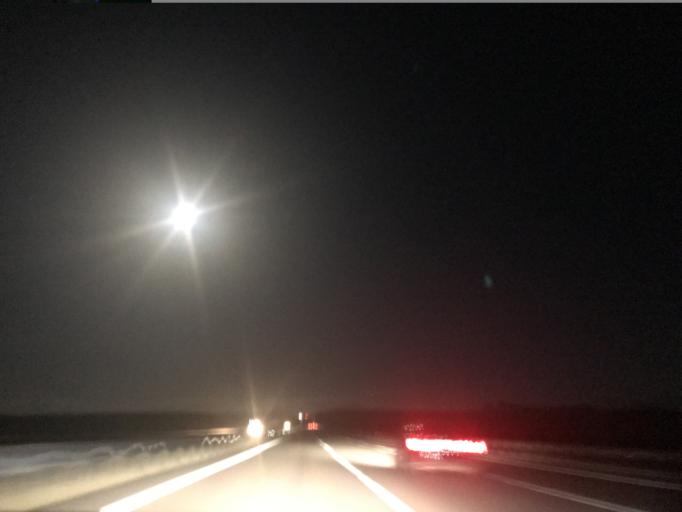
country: TR
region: Nigde
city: Ulukisla
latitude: 37.6392
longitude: 34.3898
